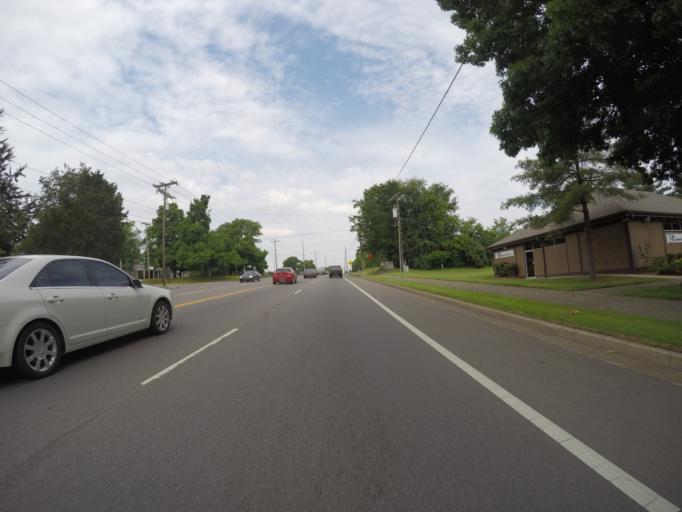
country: US
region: Tennessee
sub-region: Davidson County
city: Goodlettsville
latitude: 36.2642
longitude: -86.7246
